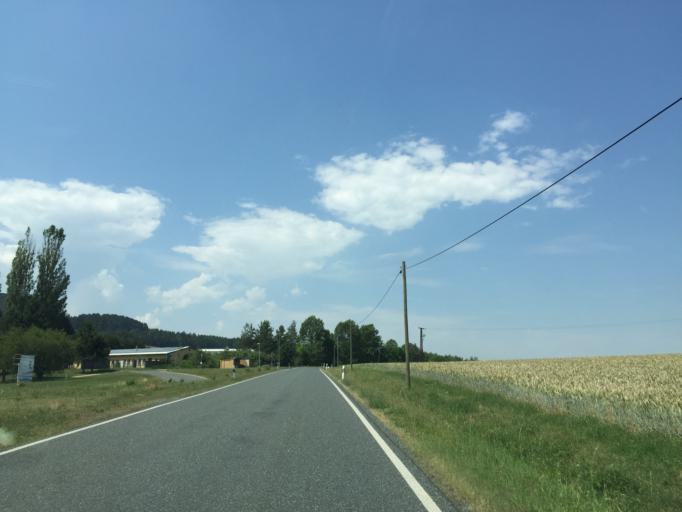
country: DE
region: Thuringia
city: Rittersdorf
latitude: 50.7801
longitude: 11.2098
